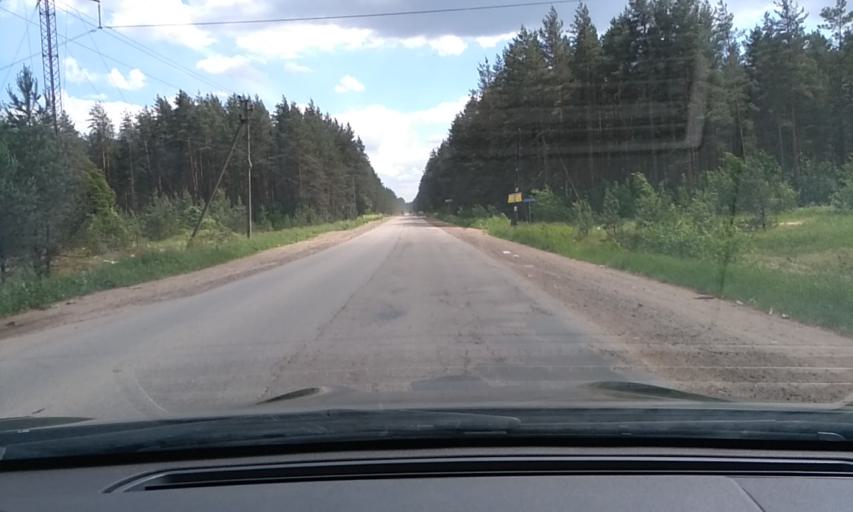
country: RU
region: Leningrad
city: Imeni Sverdlova
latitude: 59.8557
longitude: 30.6740
